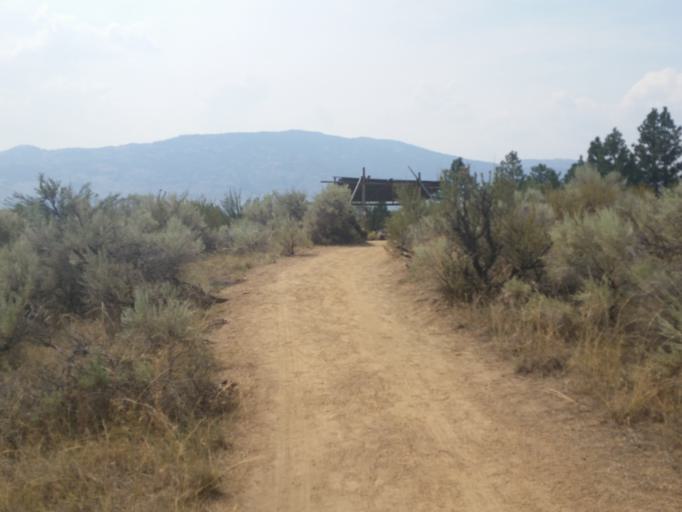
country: CA
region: British Columbia
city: Osoyoos
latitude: 49.0433
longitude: -119.4343
